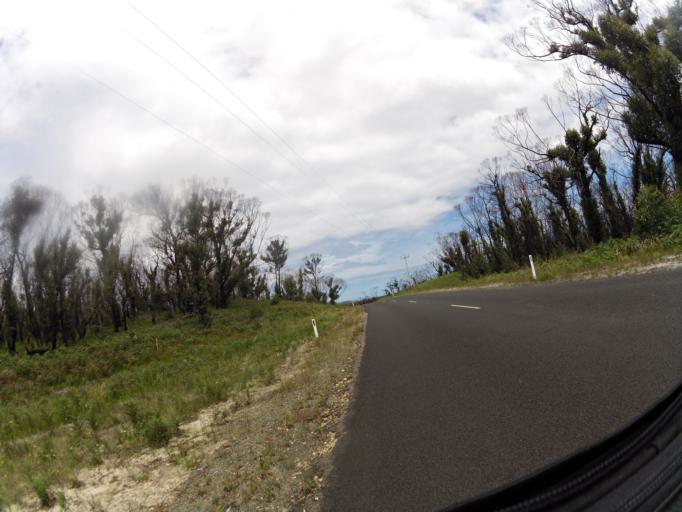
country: AU
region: Victoria
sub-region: East Gippsland
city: Lakes Entrance
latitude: -37.7936
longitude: 148.7307
